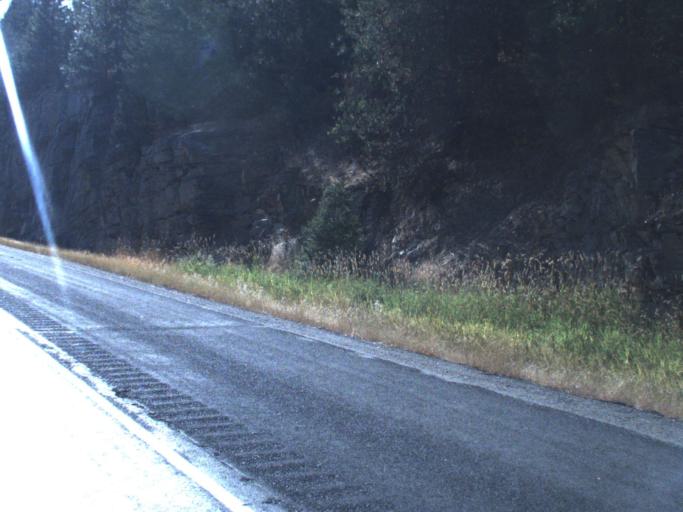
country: US
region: Washington
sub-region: Spokane County
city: Deer Park
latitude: 48.0971
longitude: -117.3085
